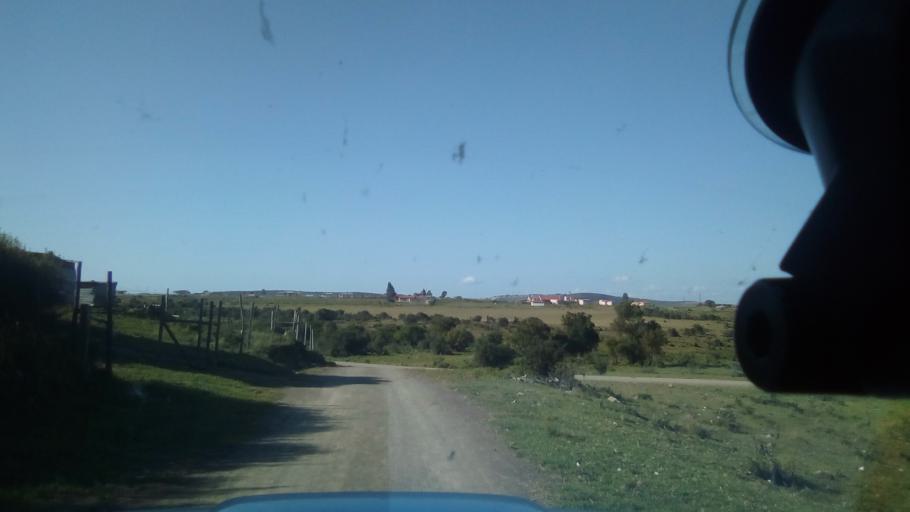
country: ZA
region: Eastern Cape
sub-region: Buffalo City Metropolitan Municipality
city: Bhisho
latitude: -32.8139
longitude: 27.3593
